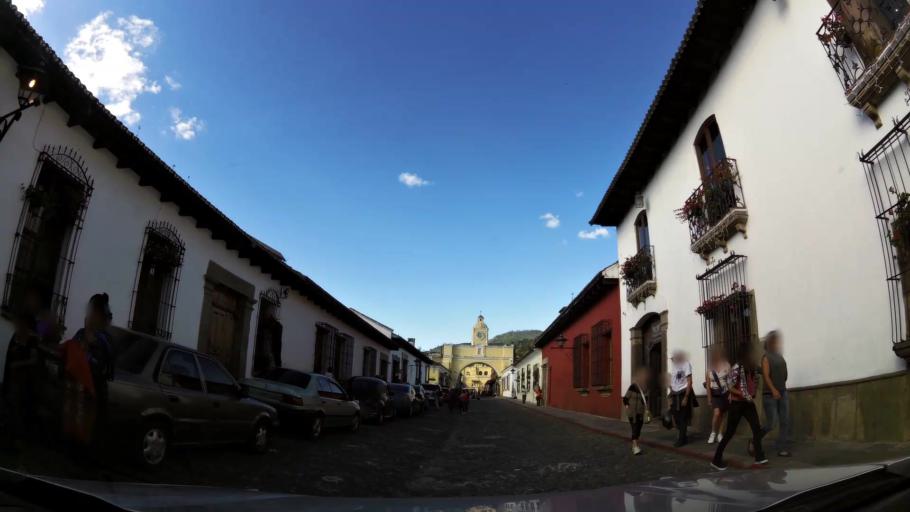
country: GT
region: Sacatepequez
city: Antigua Guatemala
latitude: 14.5587
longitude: -90.7343
